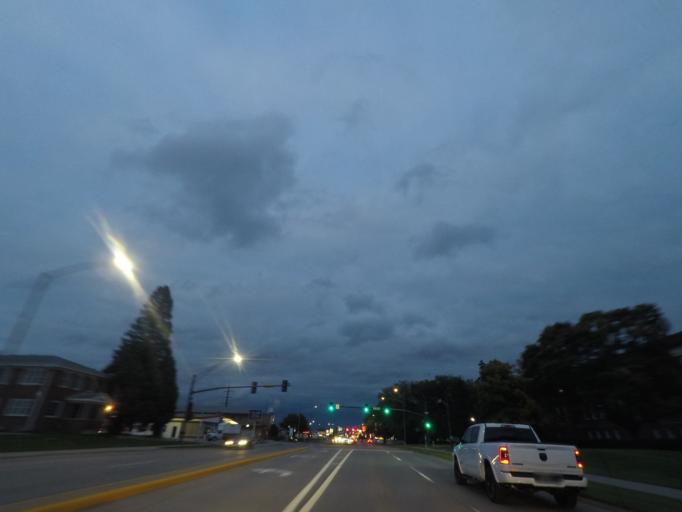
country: US
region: Iowa
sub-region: Story County
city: Ames
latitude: 42.0228
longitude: -93.6228
